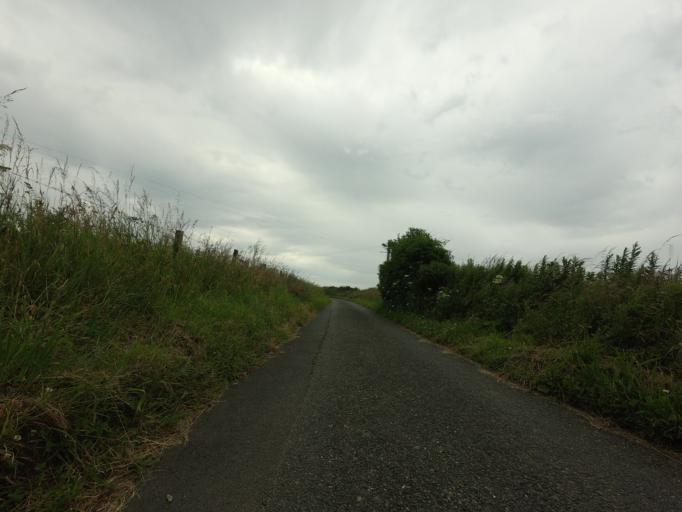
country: GB
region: Scotland
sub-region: Aberdeenshire
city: Whitehills
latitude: 57.6732
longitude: -2.5983
